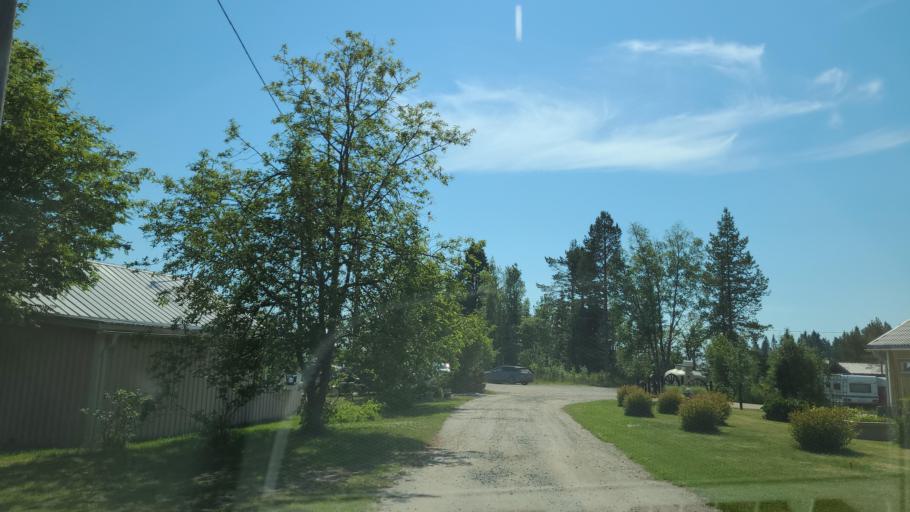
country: SE
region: Vaesterbotten
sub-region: Robertsfors Kommun
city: Robertsfors
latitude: 64.1429
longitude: 20.9647
